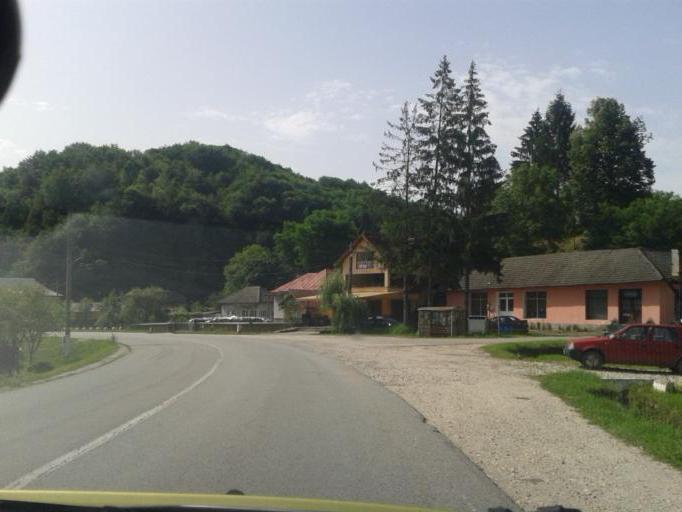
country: RO
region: Valcea
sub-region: Comuna Pietrari
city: Pietrarii de Sus
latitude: 45.1310
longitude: 24.0874
